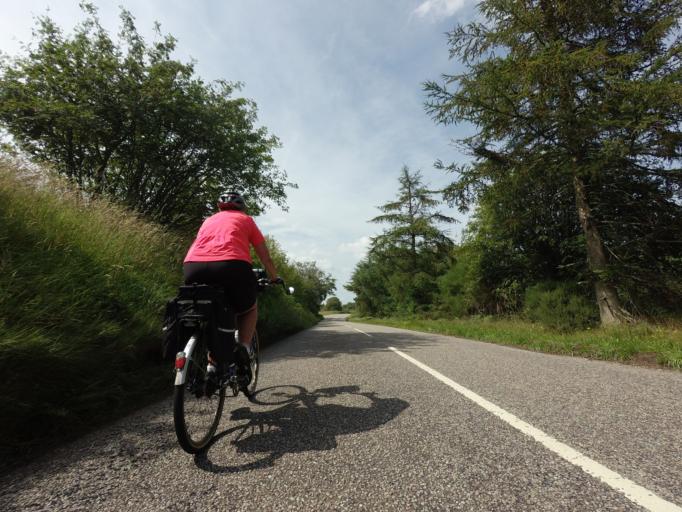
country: GB
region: Scotland
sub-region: Highland
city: Alness
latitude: 57.8565
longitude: -4.2280
